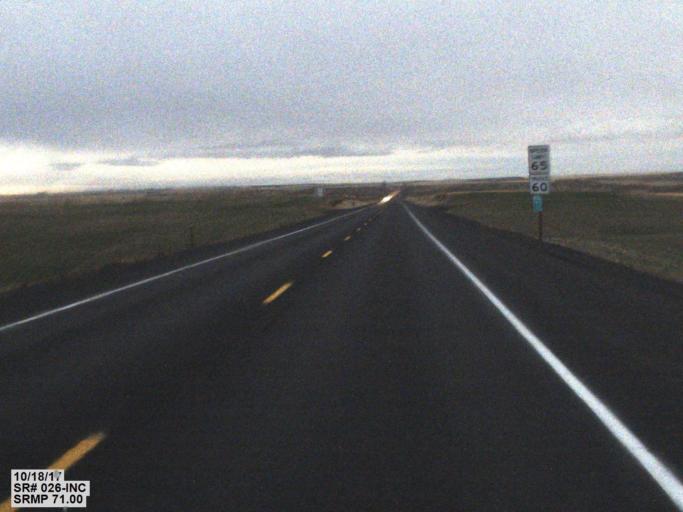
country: US
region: Washington
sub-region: Franklin County
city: Connell
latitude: 46.7949
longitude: -118.5387
